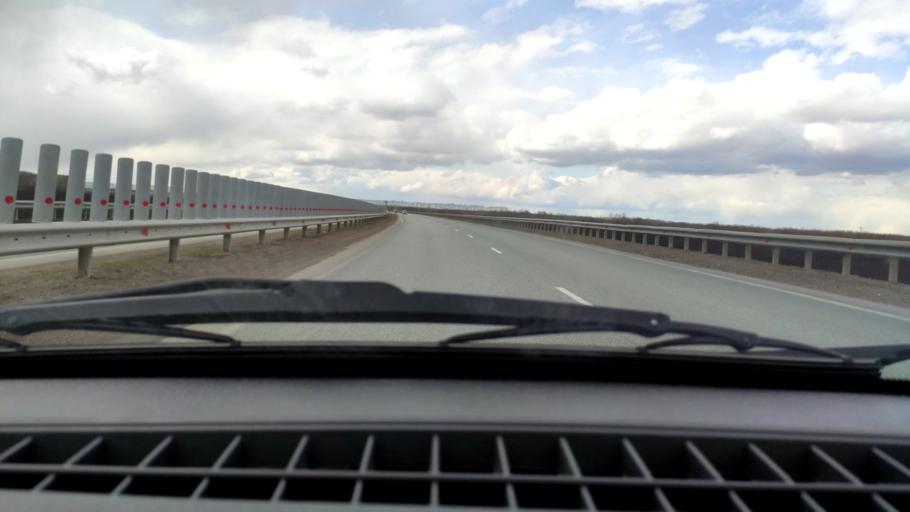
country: RU
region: Bashkortostan
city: Asanovo
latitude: 54.9758
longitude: 55.5719
